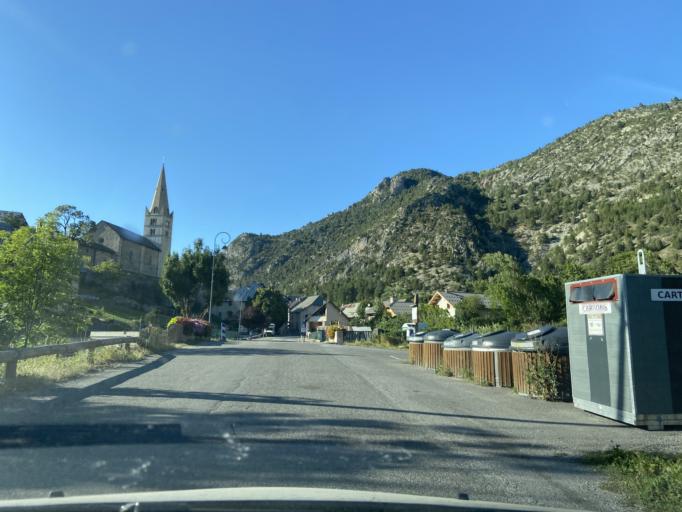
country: FR
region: Provence-Alpes-Cote d'Azur
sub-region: Departement des Hautes-Alpes
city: Guillestre
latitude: 44.7049
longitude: 6.6085
